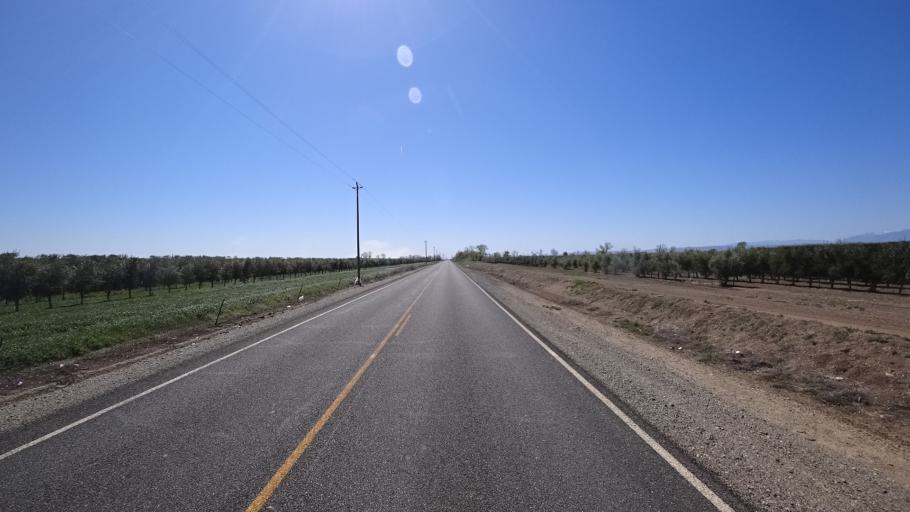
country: US
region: California
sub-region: Glenn County
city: Willows
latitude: 39.6108
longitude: -122.2499
